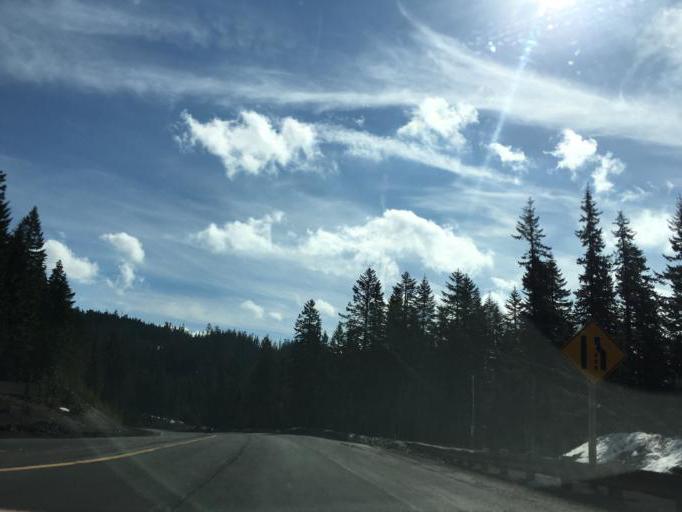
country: US
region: Oregon
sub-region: Clackamas County
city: Mount Hood Village
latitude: 45.3015
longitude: -121.7413
